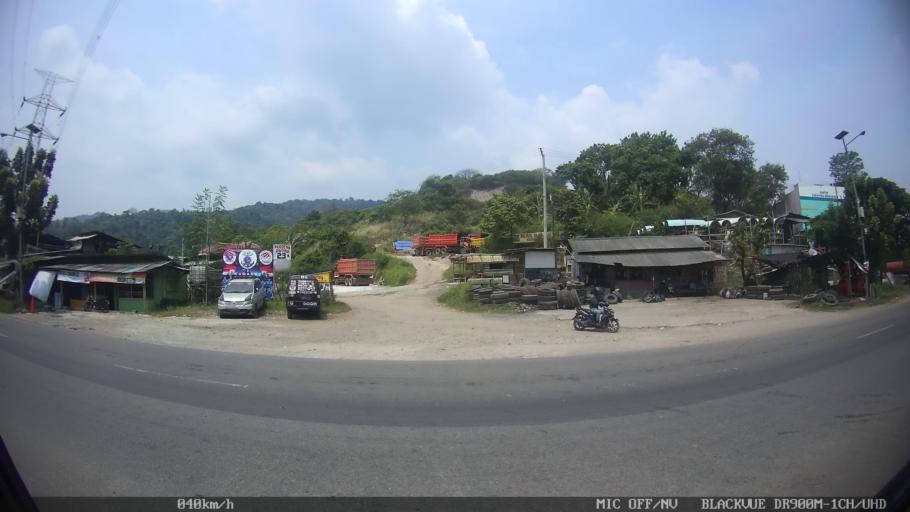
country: ID
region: Banten
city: Curug
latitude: -5.9678
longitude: 106.0059
